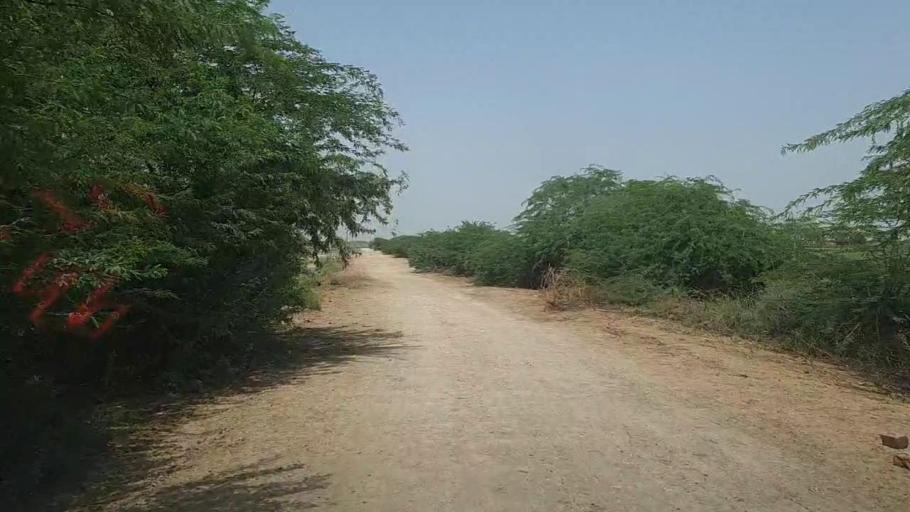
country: PK
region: Sindh
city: Pad Idan
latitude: 26.8497
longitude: 68.2954
